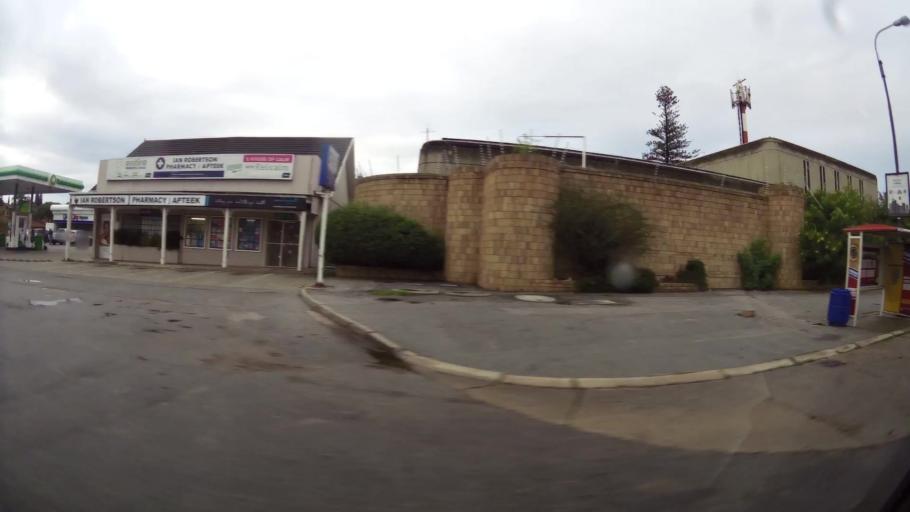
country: ZA
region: Eastern Cape
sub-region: Nelson Mandela Bay Metropolitan Municipality
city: Port Elizabeth
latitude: -33.9808
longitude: 25.5792
